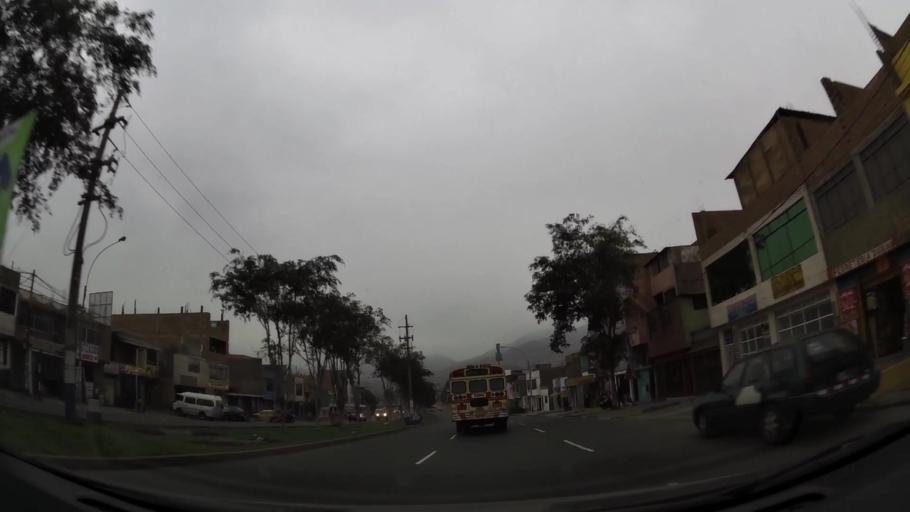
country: PE
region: Lima
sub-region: Lima
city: Independencia
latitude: -11.9369
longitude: -77.0801
